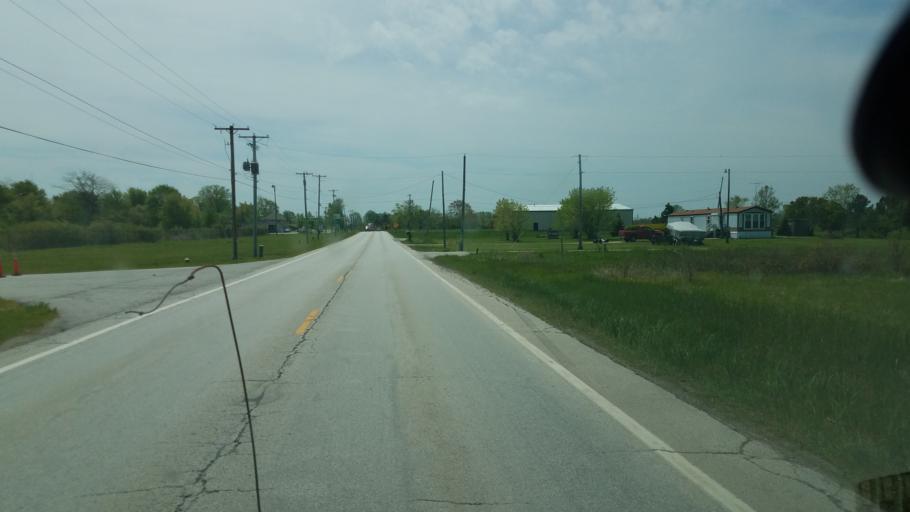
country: US
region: Ohio
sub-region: Ottawa County
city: Oak Harbor
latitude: 41.5909
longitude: -83.0967
